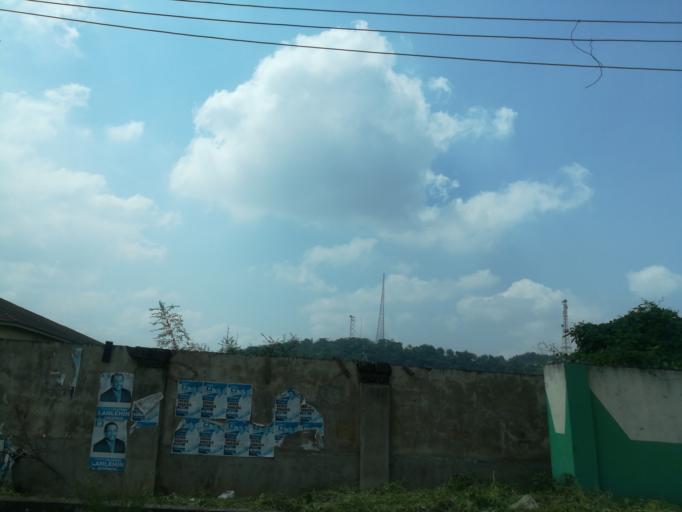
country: NG
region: Oyo
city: Ibadan
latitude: 7.3997
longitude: 3.8998
